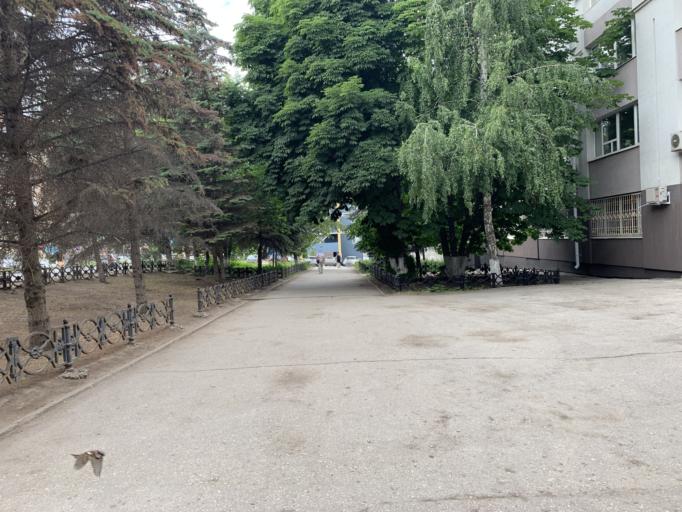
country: RU
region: Samara
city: Samara
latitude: 53.2131
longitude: 50.1692
